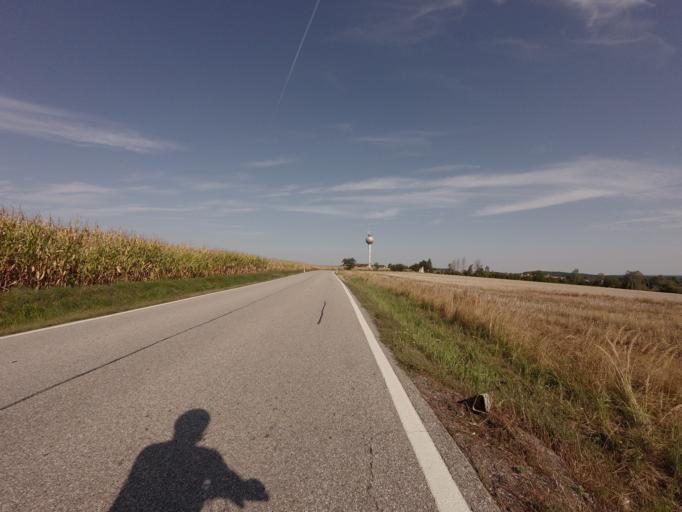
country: CZ
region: Jihocesky
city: Bernartice
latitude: 49.3011
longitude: 14.3835
